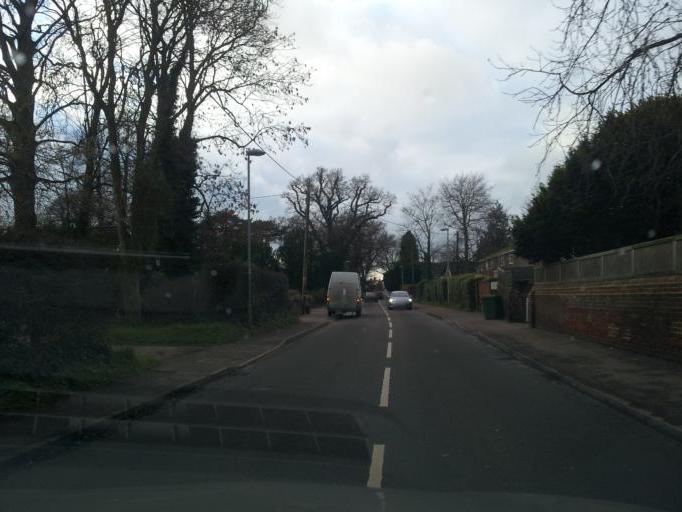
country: GB
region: England
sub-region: Norfolk
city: Brundall
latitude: 52.6246
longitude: 1.4311
